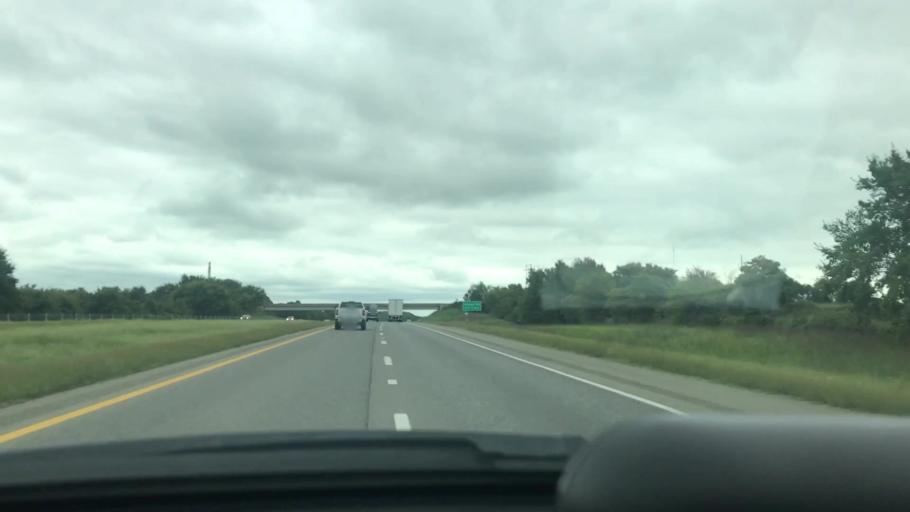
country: US
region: Oklahoma
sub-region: McIntosh County
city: Checotah
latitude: 35.3883
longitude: -95.5664
